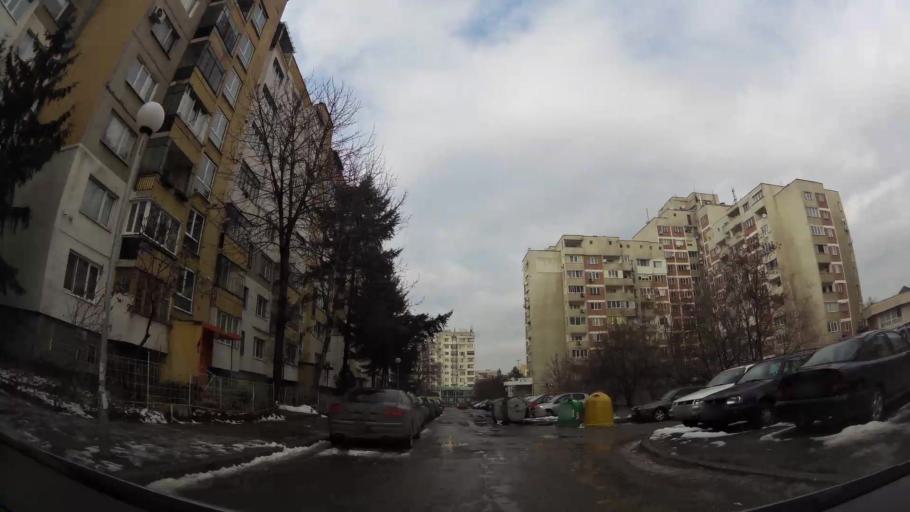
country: BG
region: Sofiya
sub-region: Obshtina Bozhurishte
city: Bozhurishte
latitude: 42.7145
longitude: 23.2519
